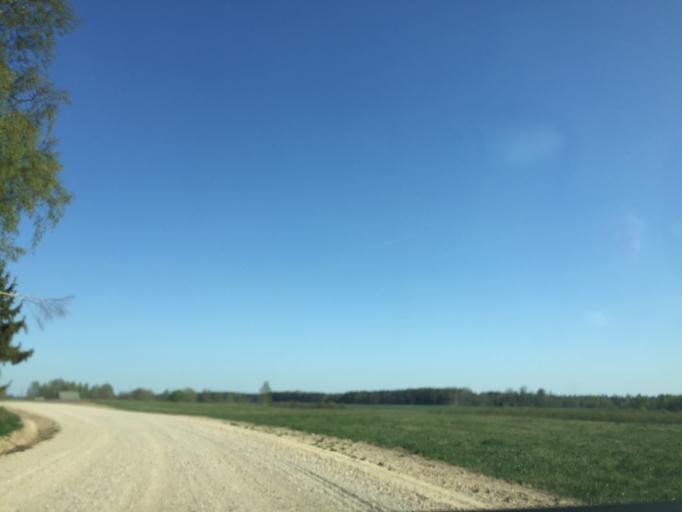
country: LV
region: Skriveri
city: Skriveri
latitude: 56.8331
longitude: 25.2192
